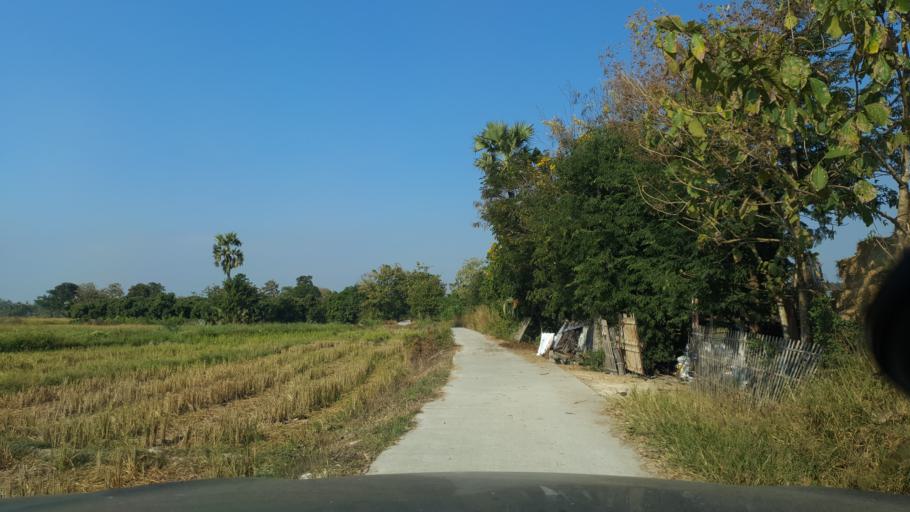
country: TH
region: Lamphun
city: Ban Thi
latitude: 18.6757
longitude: 99.1384
